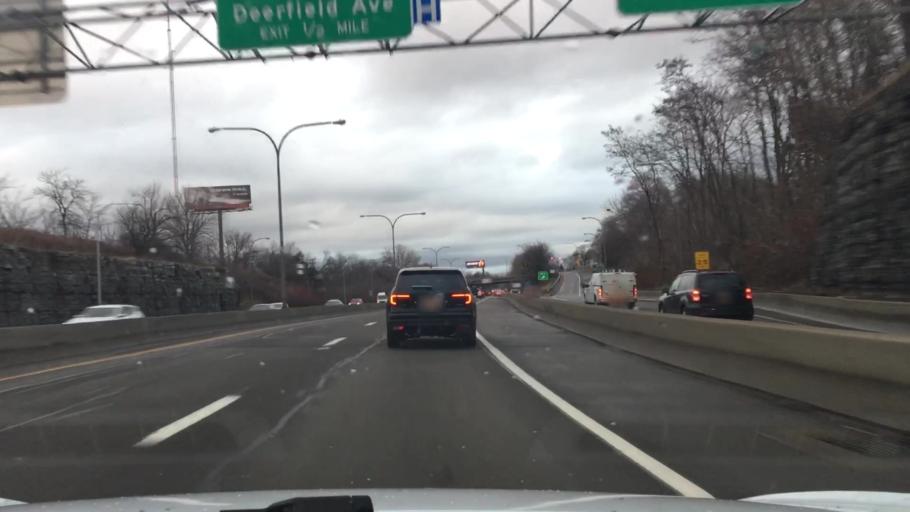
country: US
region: New York
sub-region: Erie County
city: Kenmore
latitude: 42.9237
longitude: -78.8424
